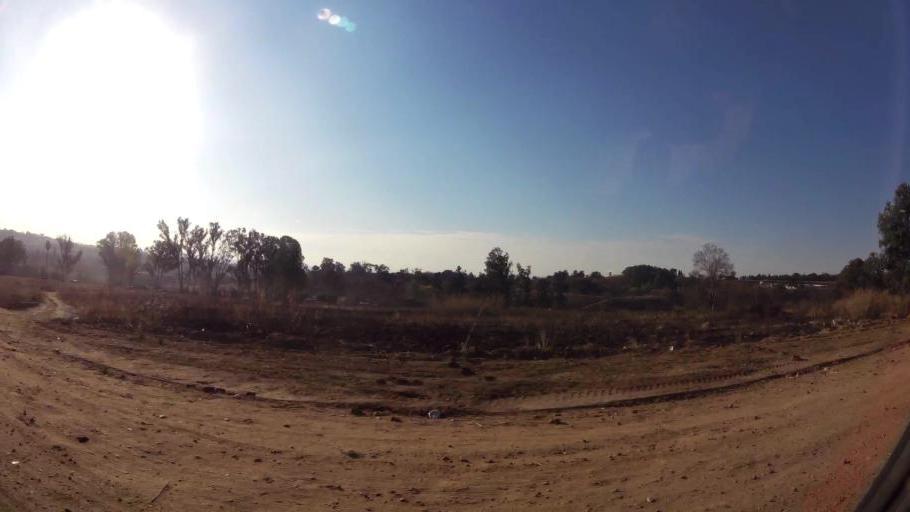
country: ZA
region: Gauteng
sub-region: West Rand District Municipality
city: Muldersdriseloop
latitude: -26.0055
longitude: 27.9113
